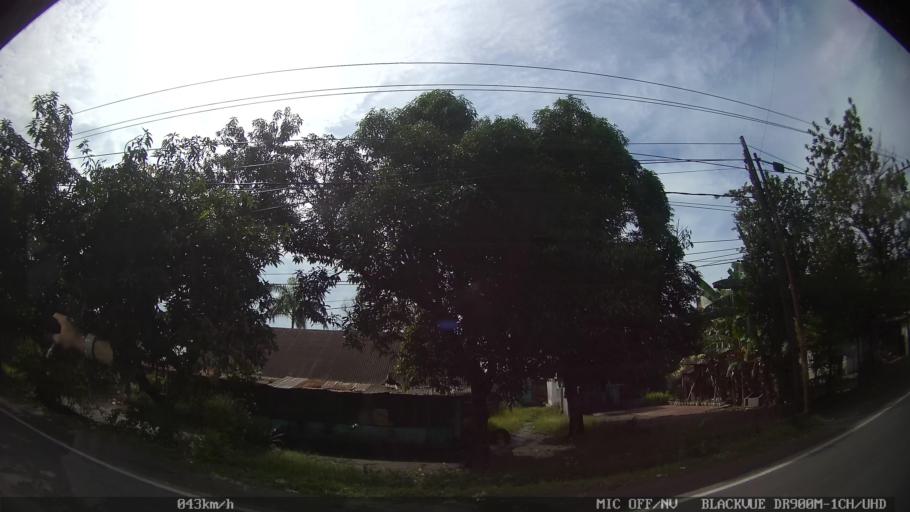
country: ID
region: North Sumatra
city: Medan
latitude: 3.6188
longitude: 98.6556
